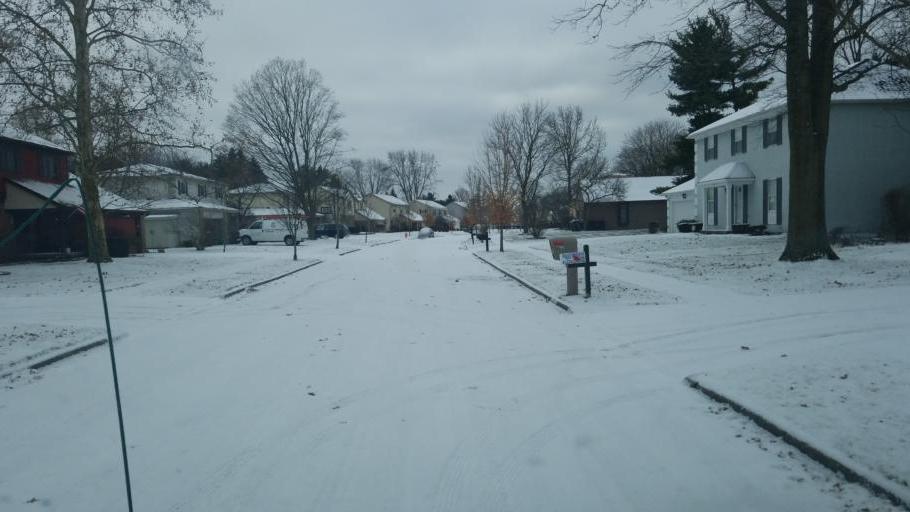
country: US
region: Ohio
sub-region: Delaware County
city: Powell
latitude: 40.1252
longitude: -83.0791
